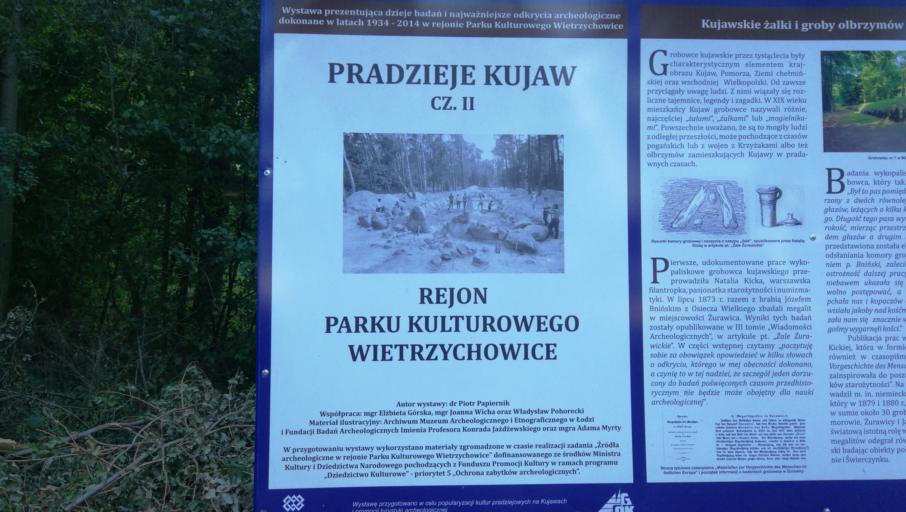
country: PL
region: Kujawsko-Pomorskie
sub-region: Powiat wloclawski
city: Boniewo
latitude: 52.4064
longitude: 18.8715
